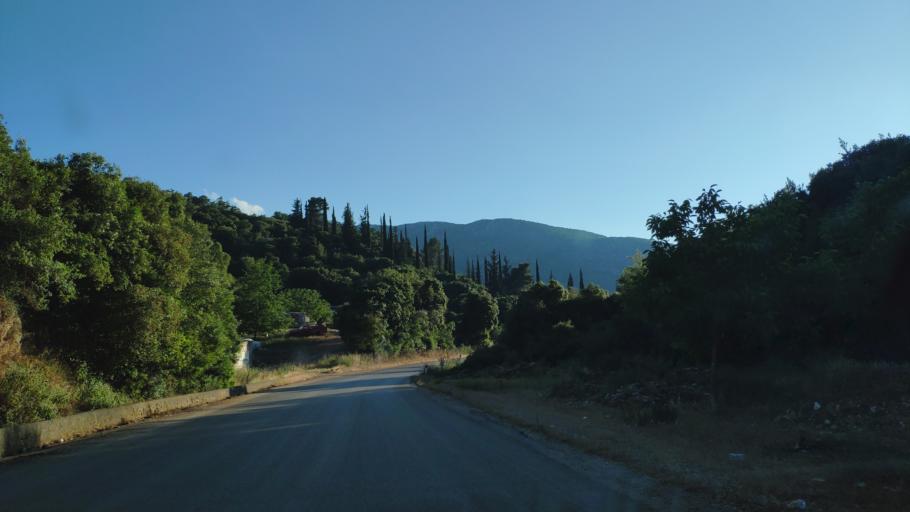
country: GR
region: West Greece
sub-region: Nomos Aitolias kai Akarnanias
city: Astakos
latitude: 38.5982
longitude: 21.0967
